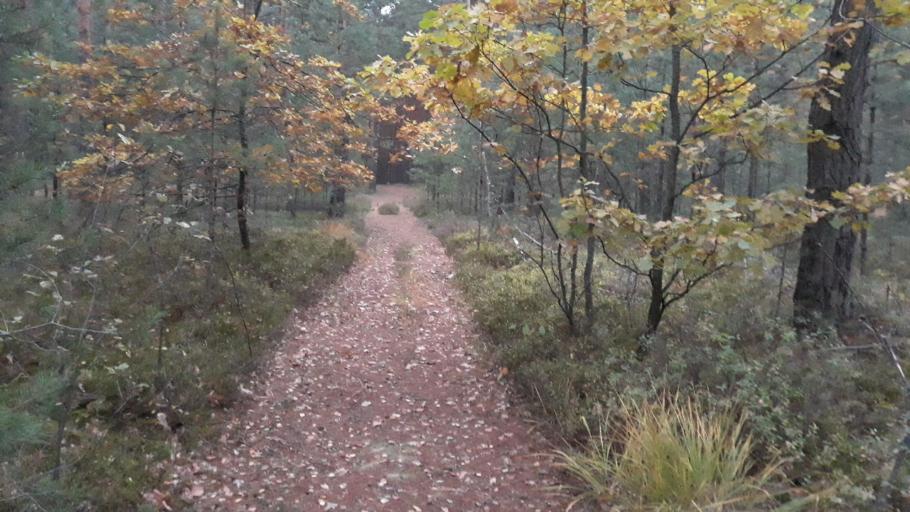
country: PL
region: Lublin Voivodeship
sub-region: Powiat janowski
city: Dzwola
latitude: 50.6474
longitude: 22.5953
